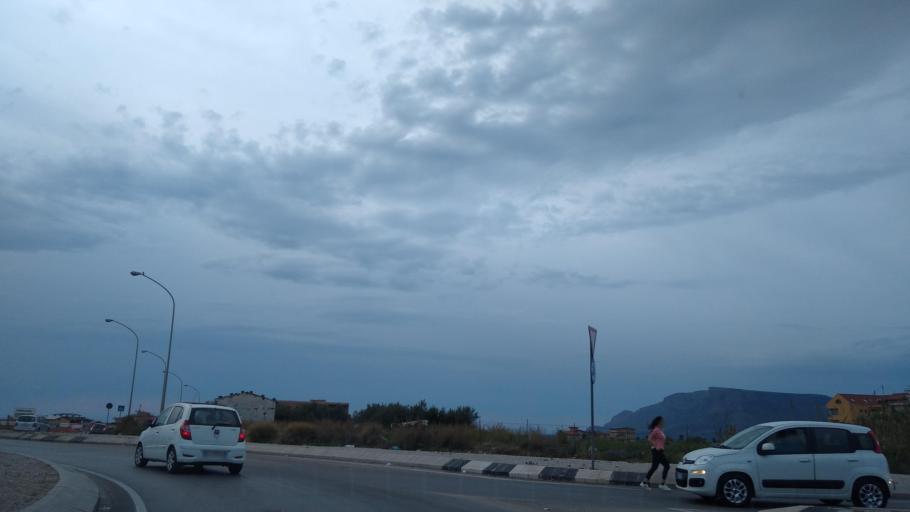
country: IT
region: Sicily
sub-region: Palermo
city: Partinico
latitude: 38.0399
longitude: 13.1082
